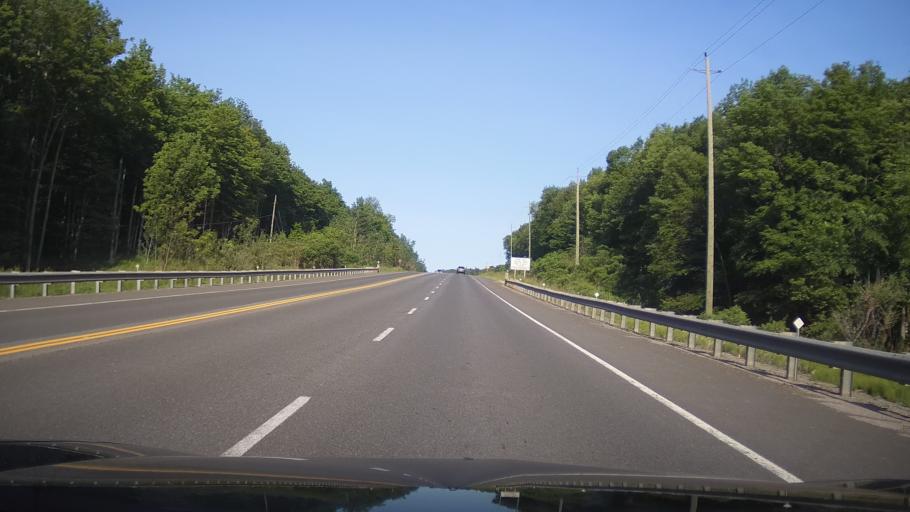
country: CA
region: Ontario
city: Quinte West
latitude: 44.5037
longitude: -77.5085
